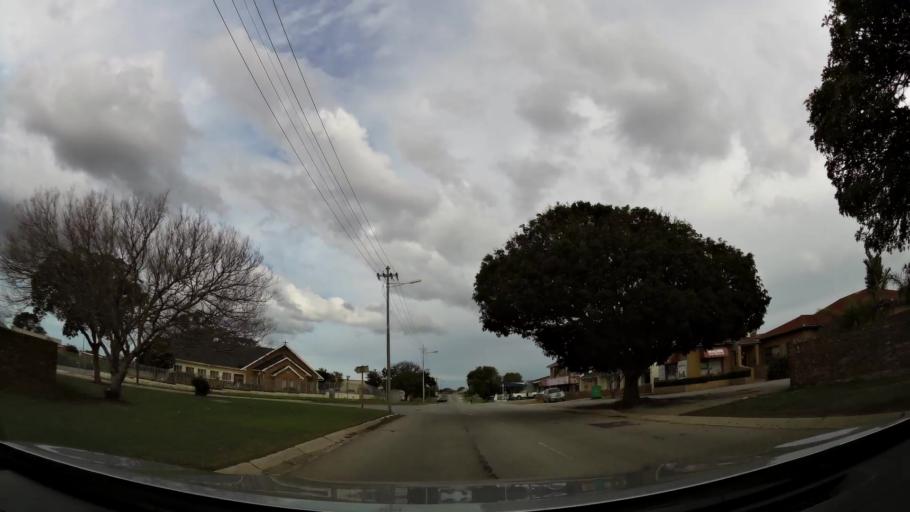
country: ZA
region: Eastern Cape
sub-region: Nelson Mandela Bay Metropolitan Municipality
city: Port Elizabeth
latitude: -33.9428
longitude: 25.5220
